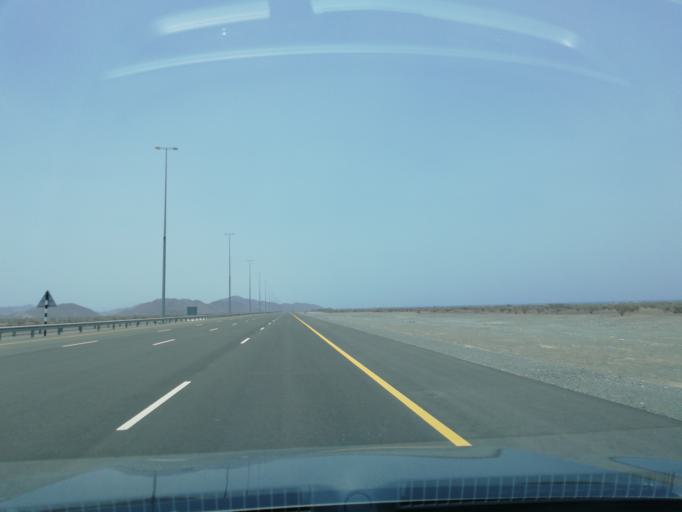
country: OM
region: Al Batinah
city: Shinas
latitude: 24.9075
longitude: 56.3548
